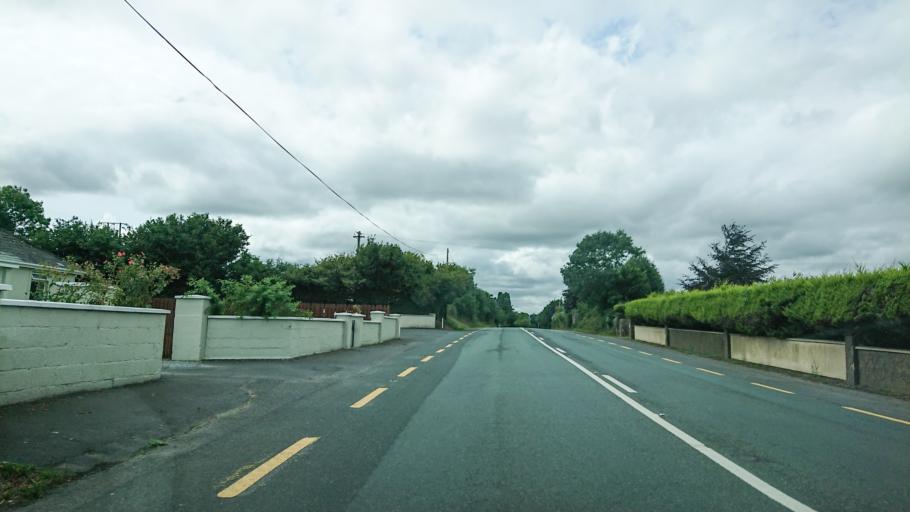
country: IE
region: Munster
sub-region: Waterford
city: Dungarvan
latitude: 52.1265
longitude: -7.7831
